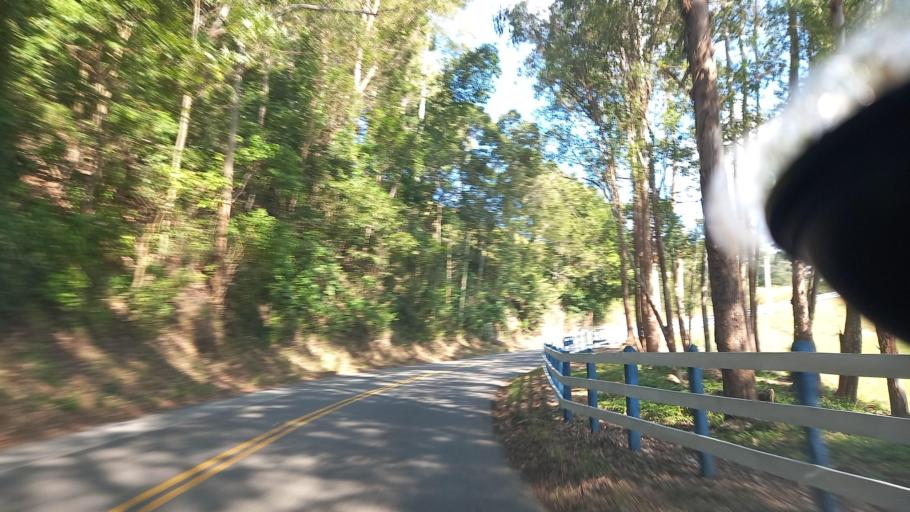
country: BR
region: Minas Gerais
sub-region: Camanducaia
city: Camanducaia
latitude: -22.7955
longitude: -46.1246
